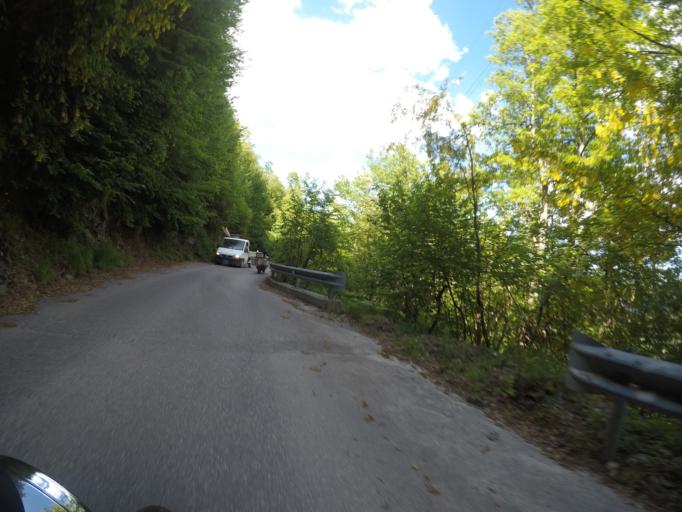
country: IT
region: Tuscany
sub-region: Provincia di Lucca
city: Minucciano
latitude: 44.1558
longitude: 10.1996
